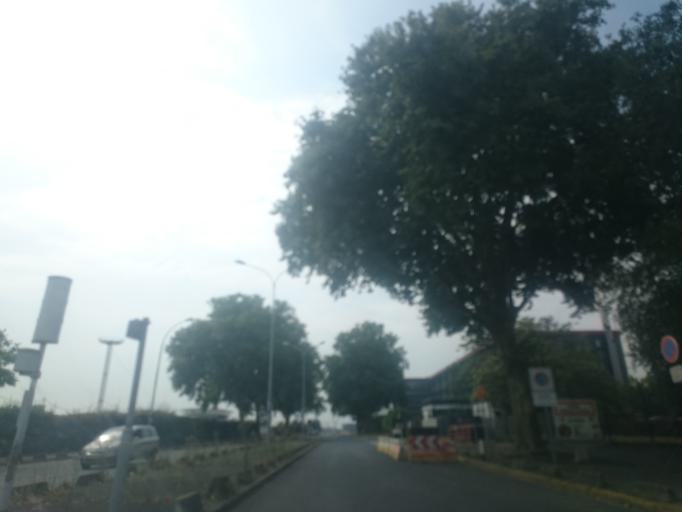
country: FR
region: Ile-de-France
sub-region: Departement du Val-de-Marne
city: Rungis
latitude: 48.7459
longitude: 2.3693
